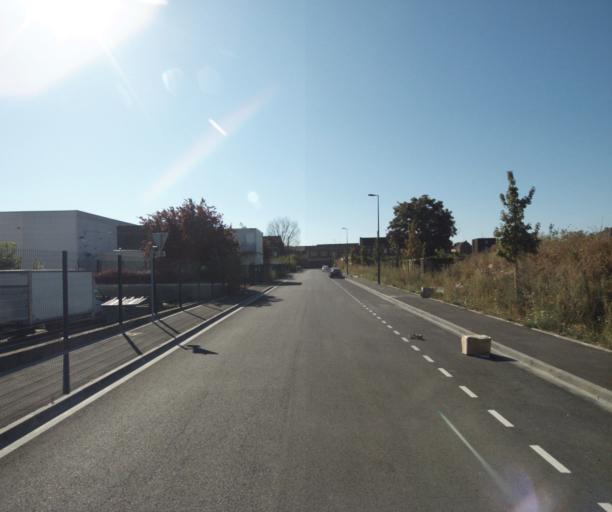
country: FR
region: Nord-Pas-de-Calais
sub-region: Departement du Nord
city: Roubaix
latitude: 50.7053
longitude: 3.1748
